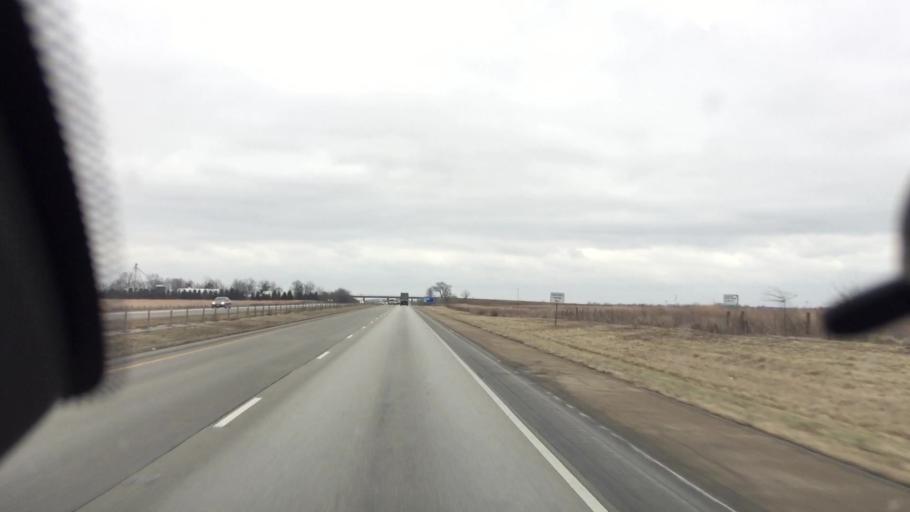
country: US
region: Illinois
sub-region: Vermilion County
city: Oakwood
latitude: 40.1266
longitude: -87.8172
